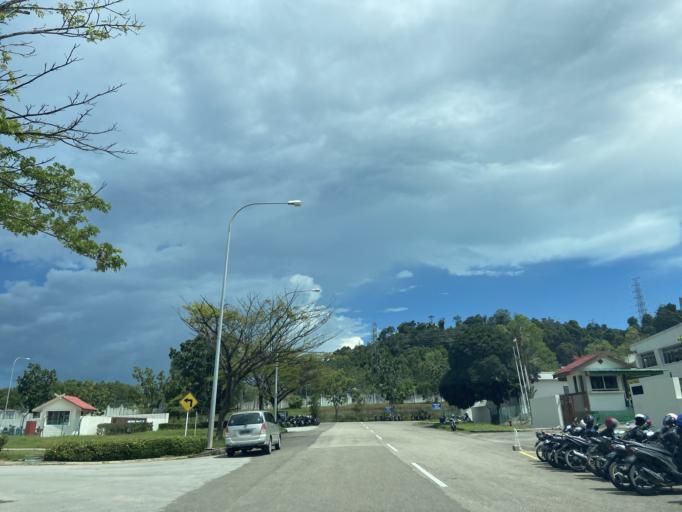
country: SG
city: Singapore
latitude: 1.0534
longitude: 104.0397
